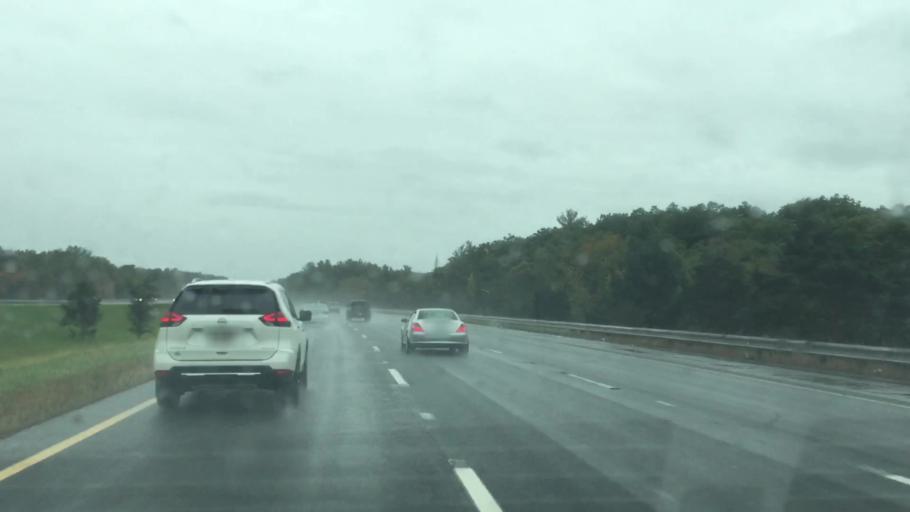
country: US
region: Massachusetts
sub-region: Essex County
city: Merrimac
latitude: 42.8065
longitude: -71.0323
